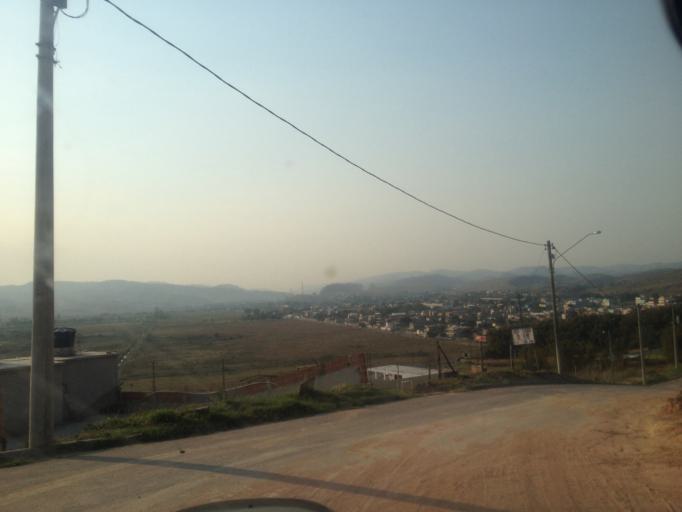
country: BR
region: Rio de Janeiro
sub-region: Porto Real
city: Porto Real
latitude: -22.4347
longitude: -44.3186
